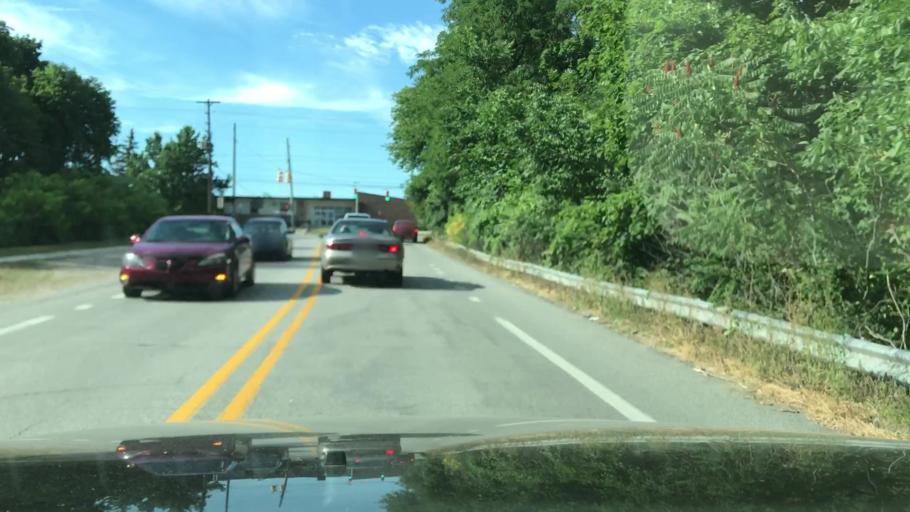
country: US
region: Michigan
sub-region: Kent County
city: East Grand Rapids
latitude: 42.9836
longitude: -85.6105
